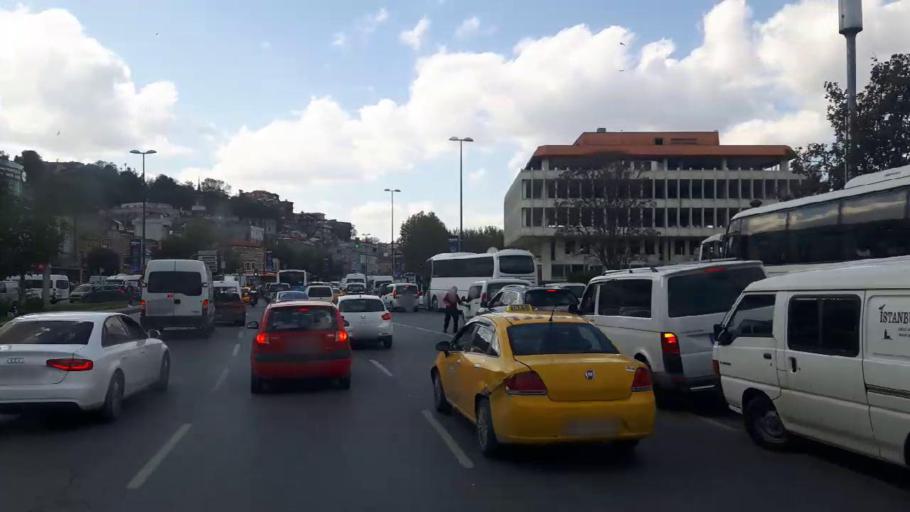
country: TR
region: Istanbul
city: Eminoenue
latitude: 41.0186
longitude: 28.9682
